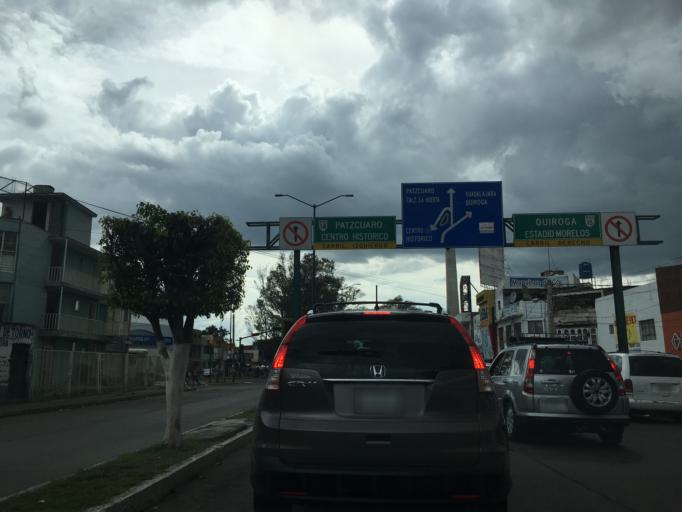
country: MX
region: Michoacan
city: Morelia
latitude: 19.7028
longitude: -101.2056
